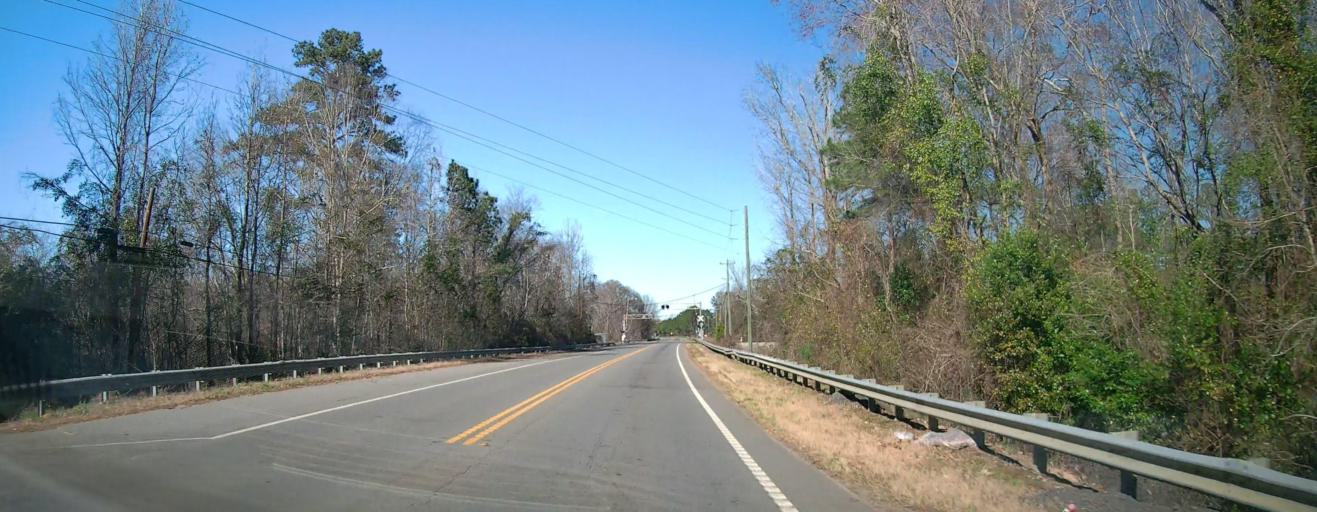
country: US
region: Georgia
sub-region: Macon County
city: Oglethorpe
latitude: 32.3089
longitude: -84.0657
